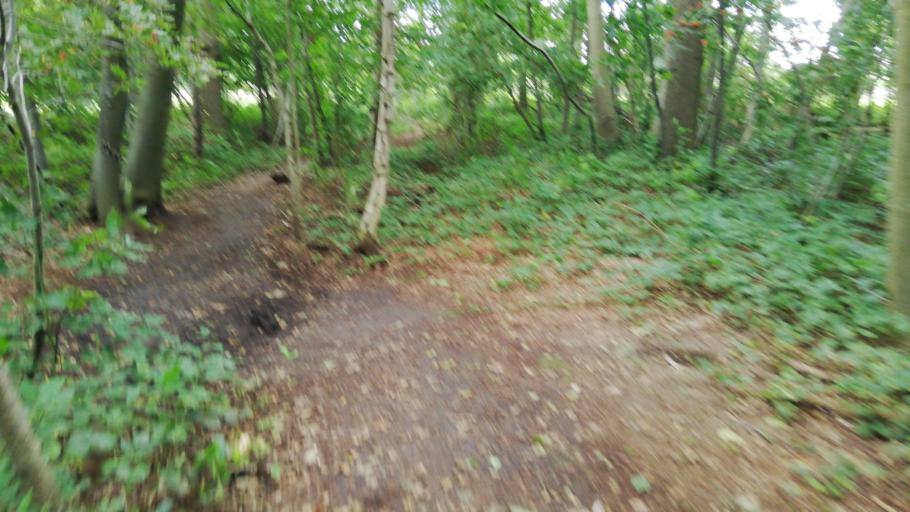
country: BE
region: Flanders
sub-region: Provincie West-Vlaanderen
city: Jabbeke
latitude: 51.1677
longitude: 3.0835
